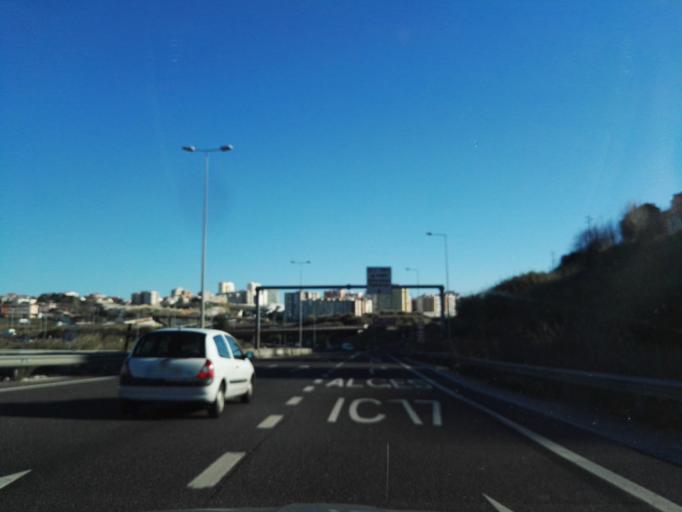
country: PT
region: Lisbon
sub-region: Odivelas
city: Pontinha
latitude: 38.7708
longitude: -9.2121
